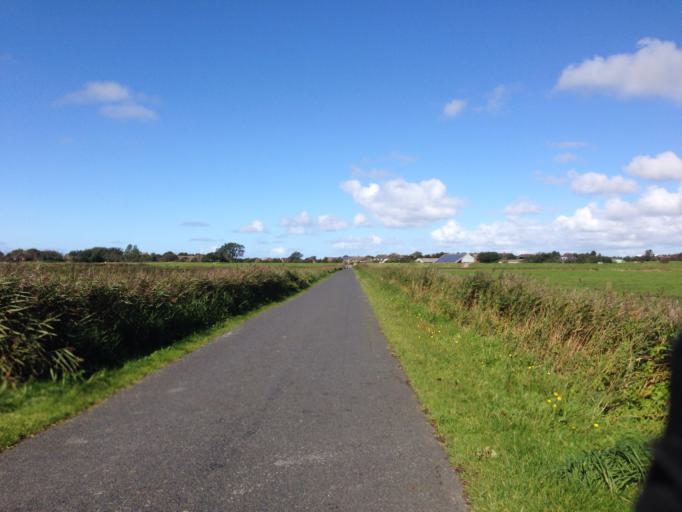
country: DE
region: Schleswig-Holstein
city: Witsum
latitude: 54.7005
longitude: 8.4235
